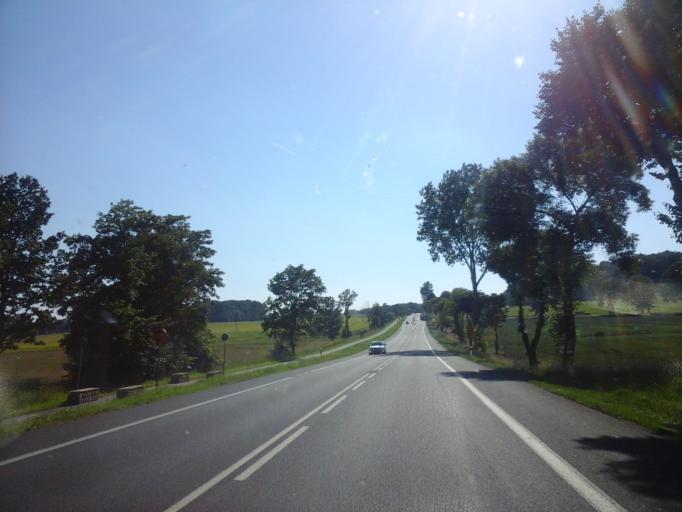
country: PL
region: West Pomeranian Voivodeship
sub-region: Powiat kolobrzeski
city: Ryman
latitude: 53.9348
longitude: 15.5069
